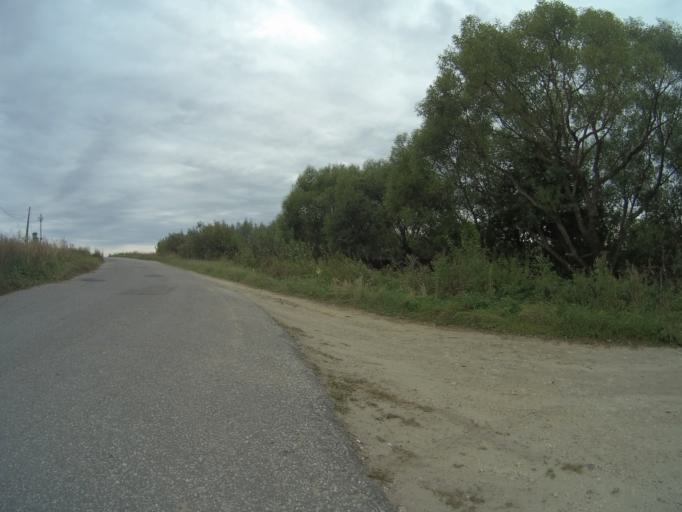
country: RU
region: Vladimir
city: Golovino
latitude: 55.9645
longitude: 40.4549
